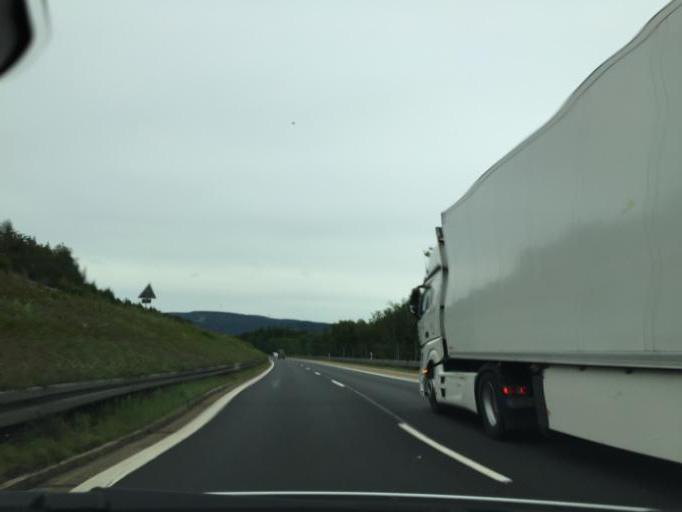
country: DE
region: Bavaria
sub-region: Regierungsbezirk Unterfranken
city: Bad Bruckenau
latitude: 50.3237
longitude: 9.7927
